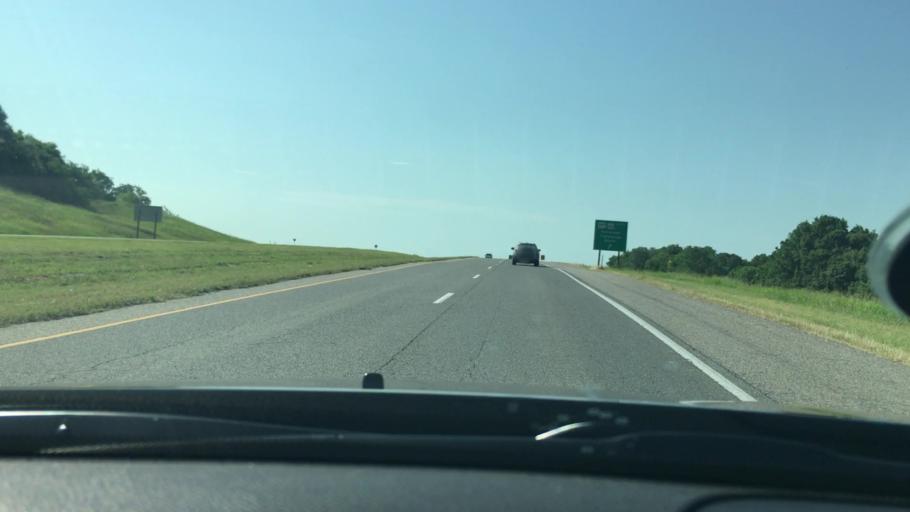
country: US
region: Oklahoma
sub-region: Pontotoc County
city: Ada
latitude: 34.7310
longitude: -96.6398
